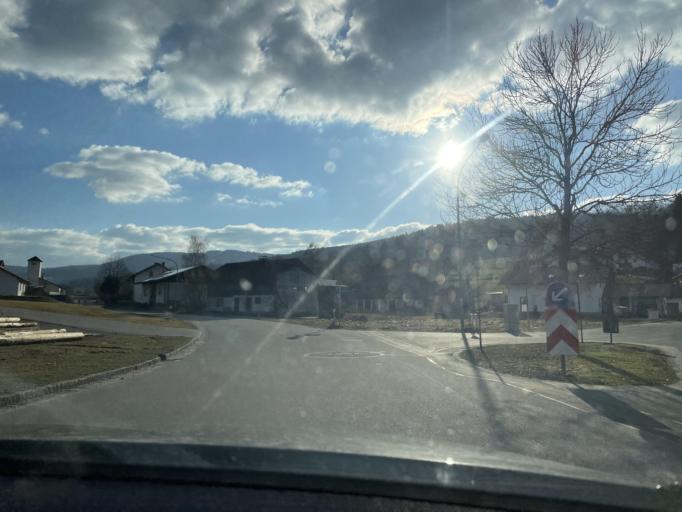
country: DE
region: Bavaria
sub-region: Lower Bavaria
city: Kollnburg
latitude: 49.0596
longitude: 12.8541
